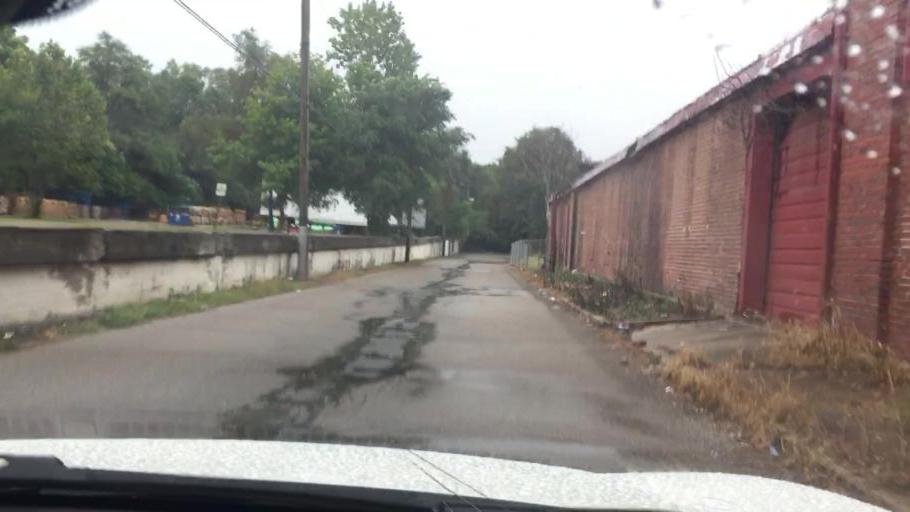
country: US
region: Ohio
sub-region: Champaign County
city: Urbana
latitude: 40.1083
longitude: -83.7590
